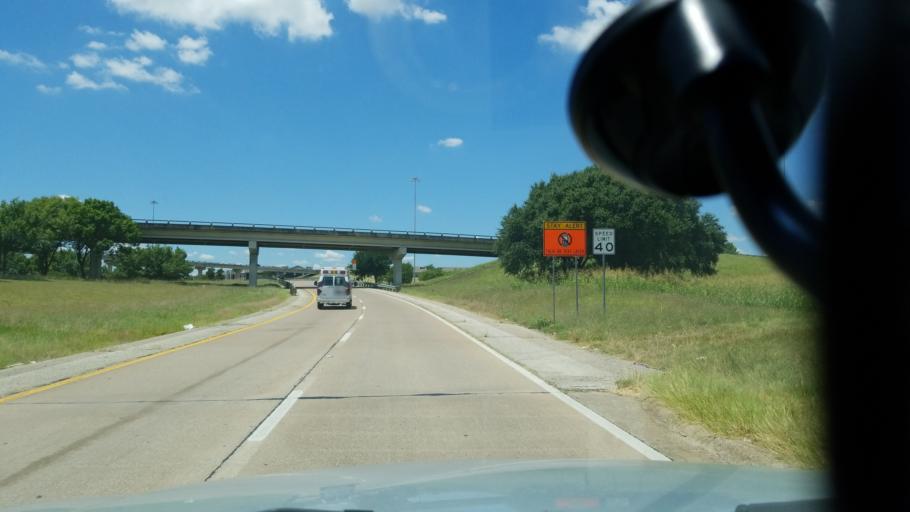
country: US
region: Texas
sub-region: Dallas County
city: Duncanville
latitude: 32.6561
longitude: -96.8777
